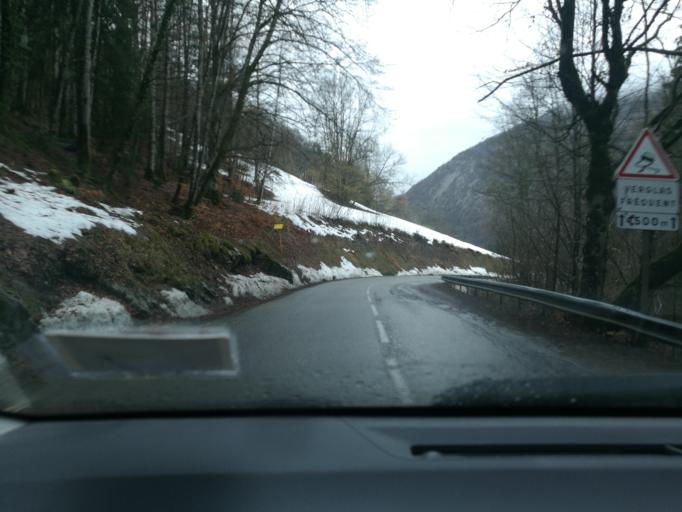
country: FR
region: Rhone-Alpes
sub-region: Departement de la Haute-Savoie
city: Araches-la-Frasse
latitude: 46.0469
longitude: 6.6256
